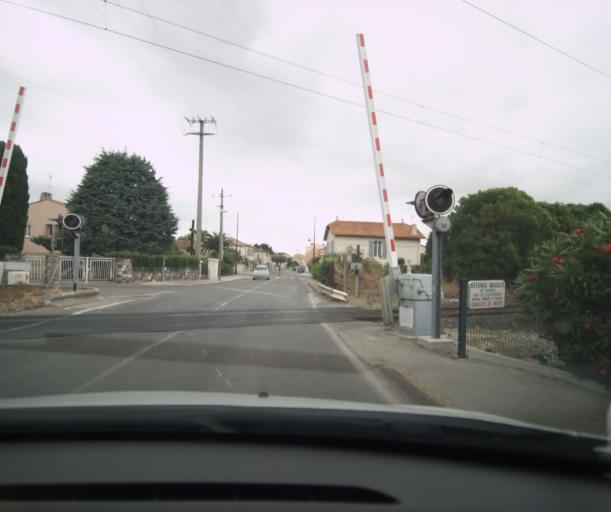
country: FR
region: Provence-Alpes-Cote d'Azur
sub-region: Departement du Var
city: La Crau
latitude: 43.1454
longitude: 6.0668
